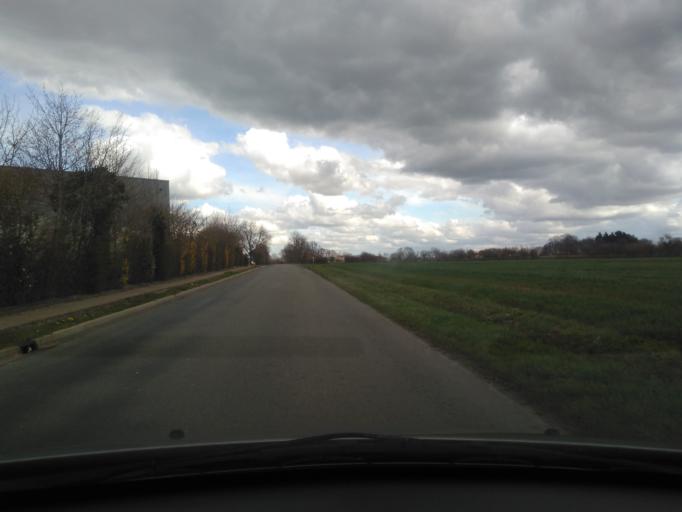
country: FR
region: Pays de la Loire
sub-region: Departement de la Vendee
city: Les Essarts
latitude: 46.7652
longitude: -1.2355
